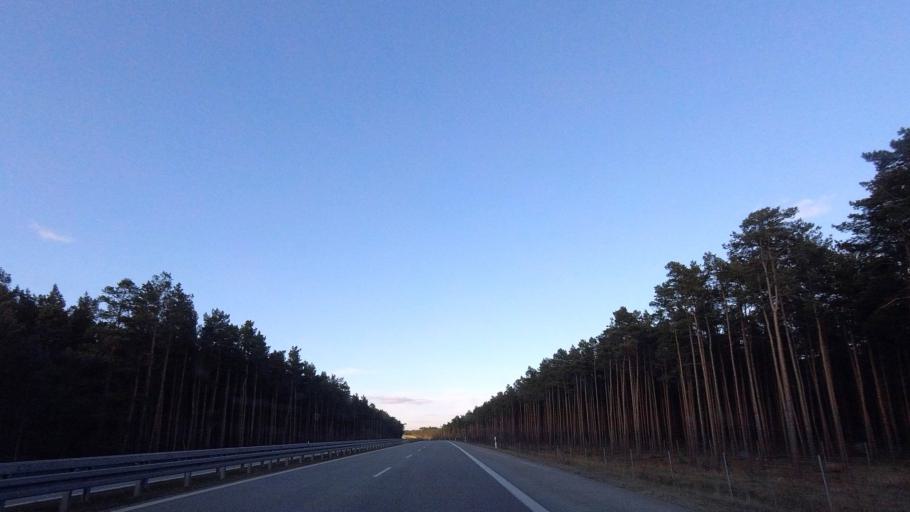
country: DE
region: Brandenburg
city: Trebbin
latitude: 52.1478
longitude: 13.2367
